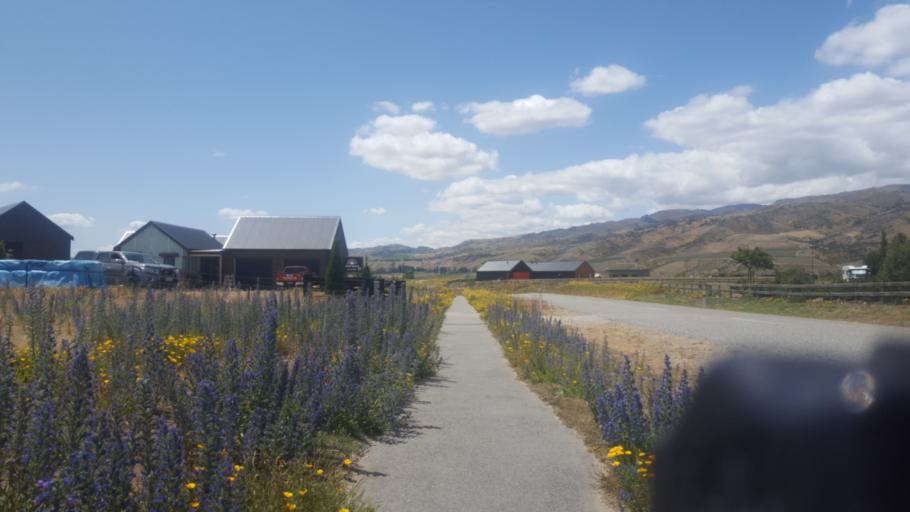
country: NZ
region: Otago
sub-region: Queenstown-Lakes District
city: Wanaka
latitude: -45.0304
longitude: 169.2044
